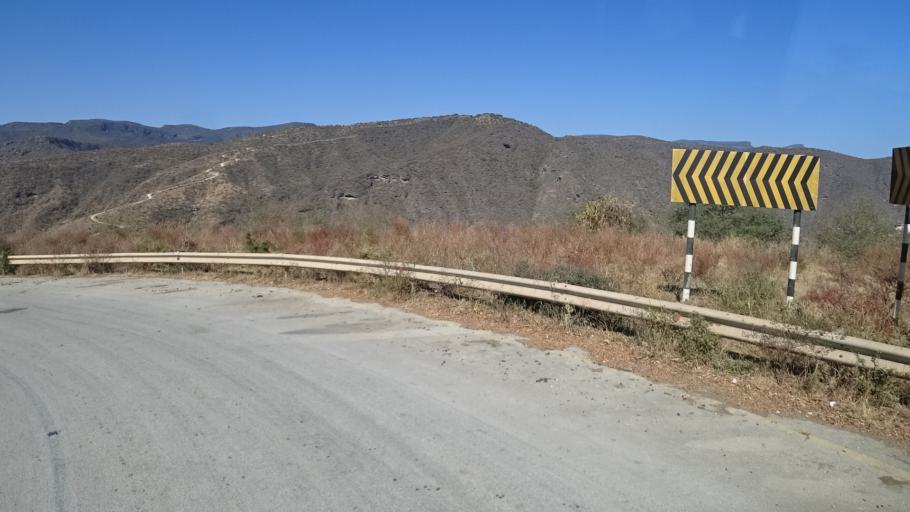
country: YE
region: Al Mahrah
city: Hawf
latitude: 16.7452
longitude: 53.4092
